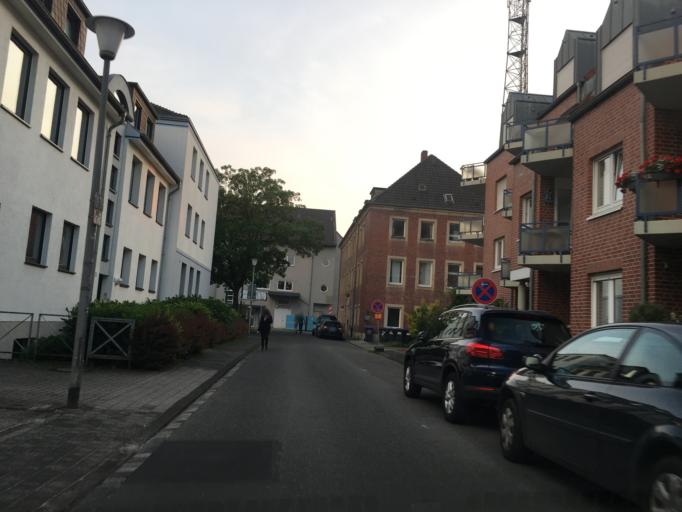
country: DE
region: North Rhine-Westphalia
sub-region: Regierungsbezirk Munster
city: Muenster
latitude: 51.9597
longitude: 7.6389
